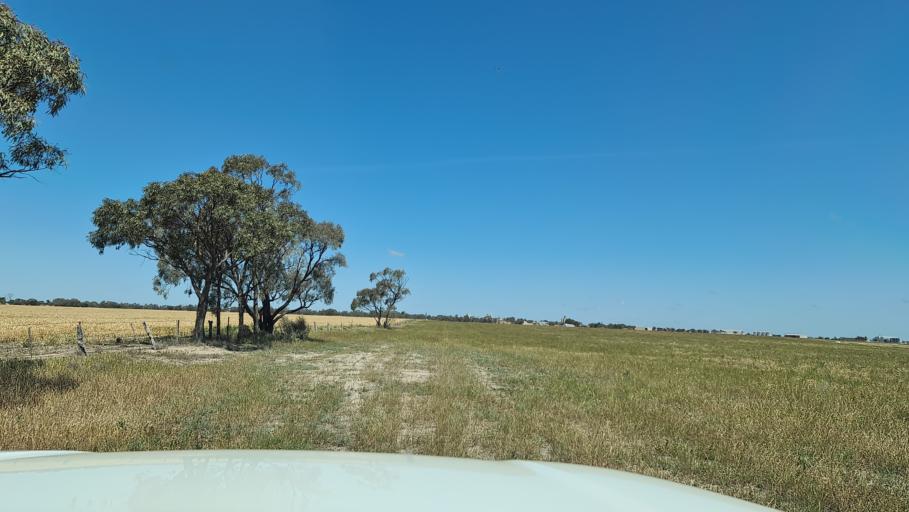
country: AU
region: Victoria
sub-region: Mildura Shire
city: Ouyen
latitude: -35.7101
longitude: 142.3640
